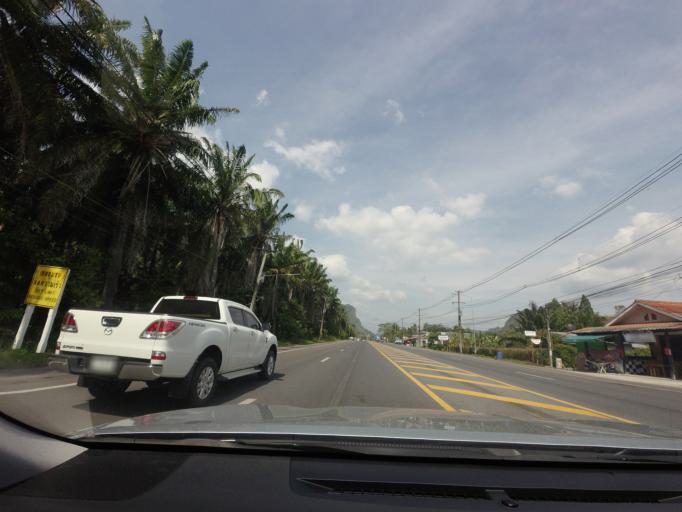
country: TH
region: Phangnga
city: Ban Ao Nang
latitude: 8.0591
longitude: 98.7825
